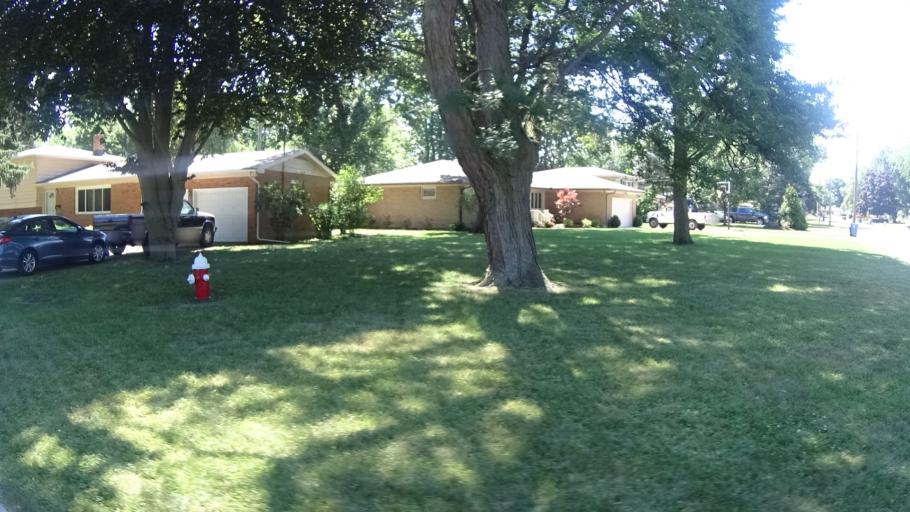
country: US
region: Ohio
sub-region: Erie County
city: Sandusky
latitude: 41.4315
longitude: -82.6810
